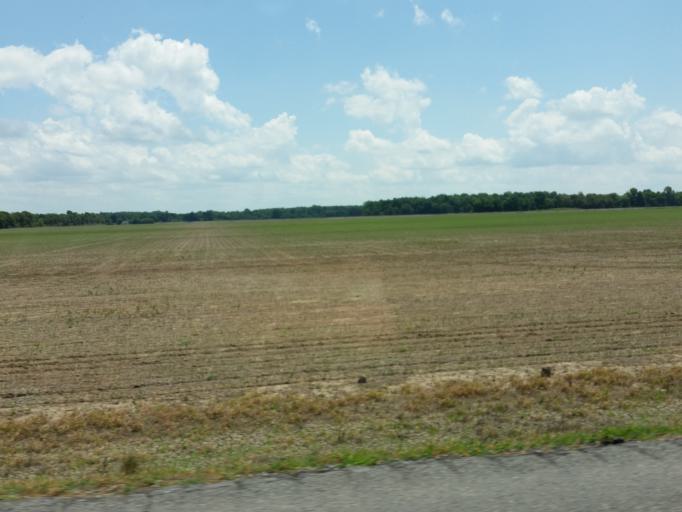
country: US
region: Kentucky
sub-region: Fulton County
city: Hickman
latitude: 36.5233
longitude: -89.3387
